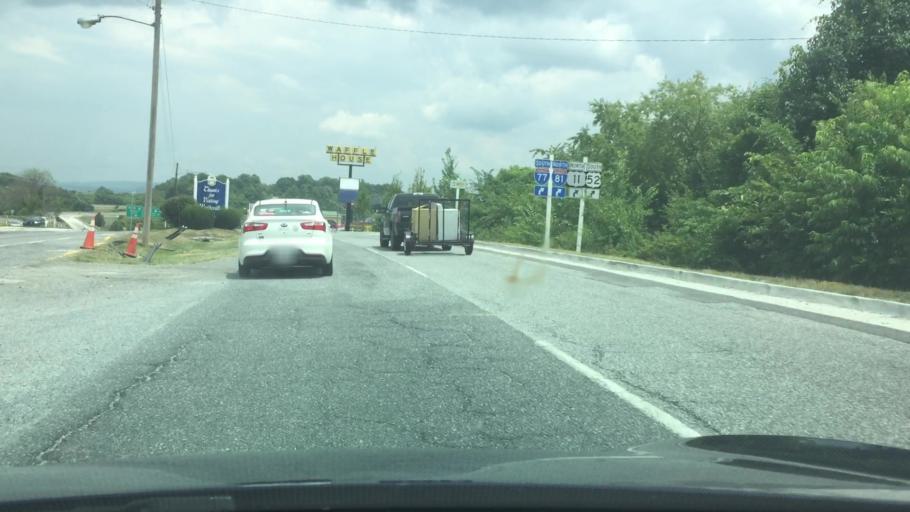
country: US
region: Virginia
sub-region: Wythe County
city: Wytheville
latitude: 36.9476
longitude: -81.0593
